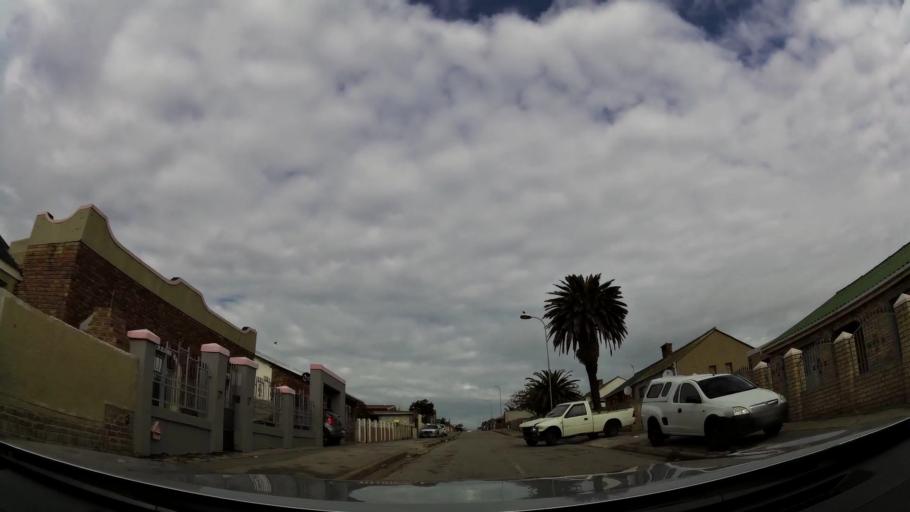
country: ZA
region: Eastern Cape
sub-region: Nelson Mandela Bay Metropolitan Municipality
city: Port Elizabeth
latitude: -33.9350
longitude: 25.5765
